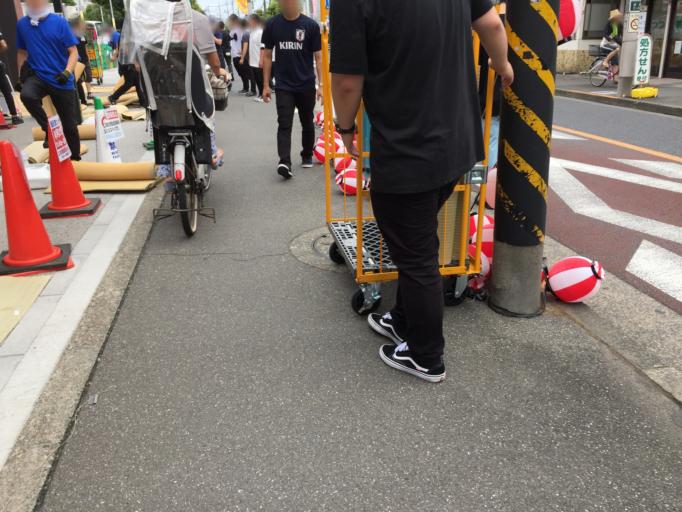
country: JP
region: Tokyo
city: Tokyo
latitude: 35.6598
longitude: 139.6429
